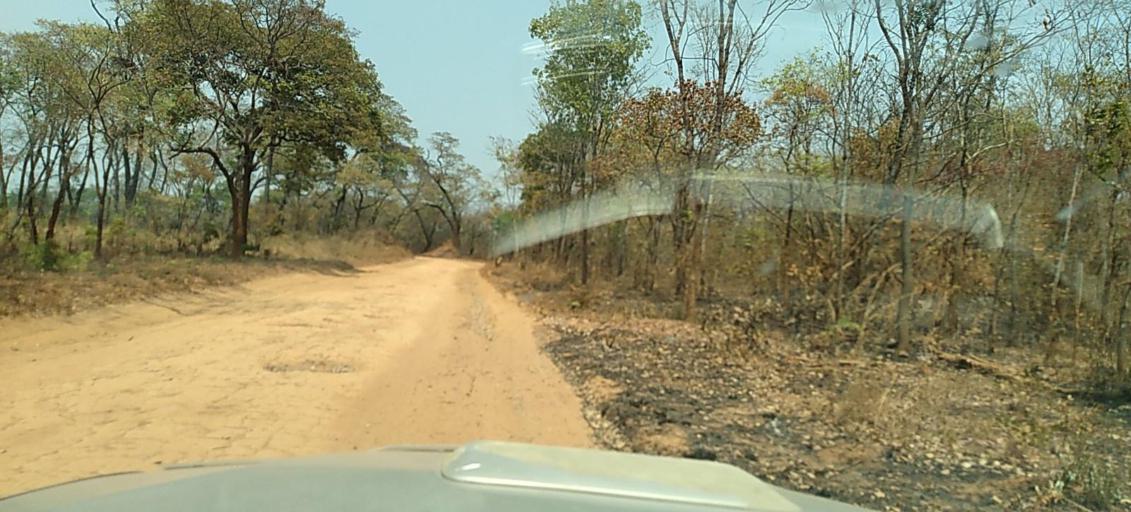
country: ZM
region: North-Western
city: Kasempa
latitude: -13.6186
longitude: 26.2021
